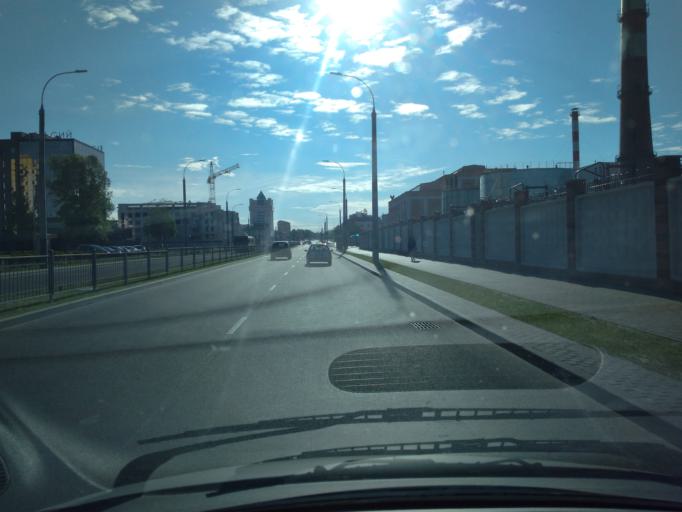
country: BY
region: Brest
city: Brest
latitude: 52.0855
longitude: 23.6761
